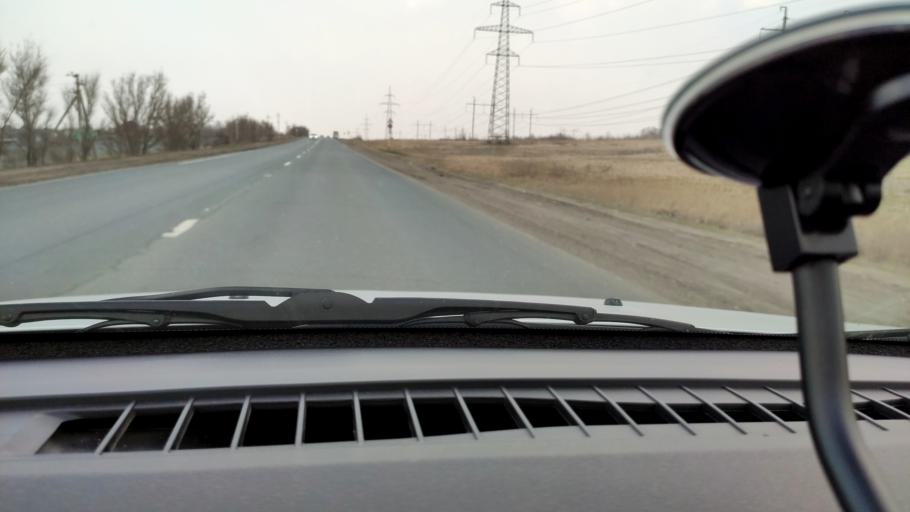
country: RU
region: Samara
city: Dubovyy Umet
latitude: 53.0658
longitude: 50.3786
